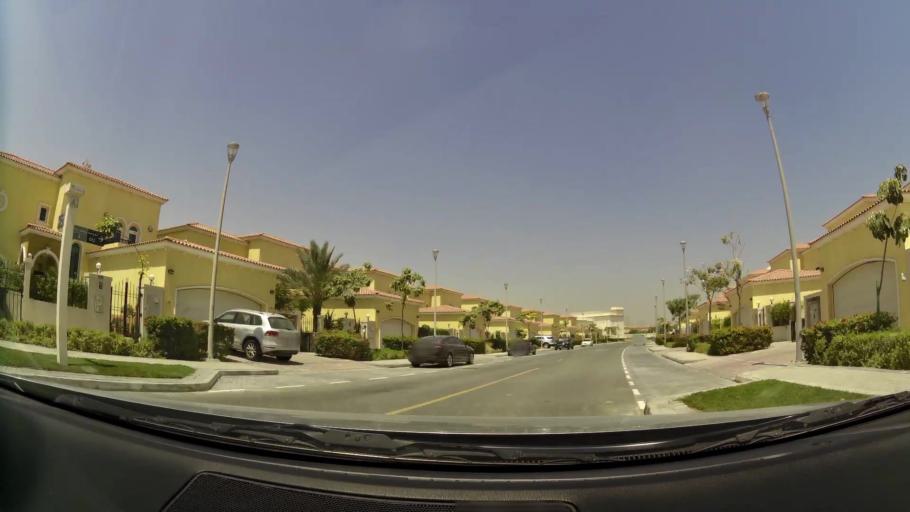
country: AE
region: Dubai
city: Dubai
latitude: 25.0375
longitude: 55.1634
